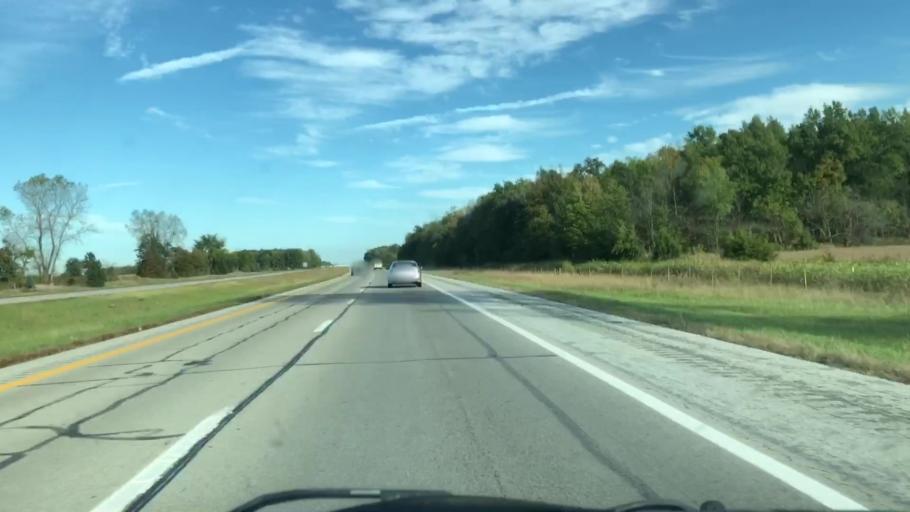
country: US
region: Ohio
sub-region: Allen County
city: Lima
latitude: 40.8240
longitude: -84.1201
